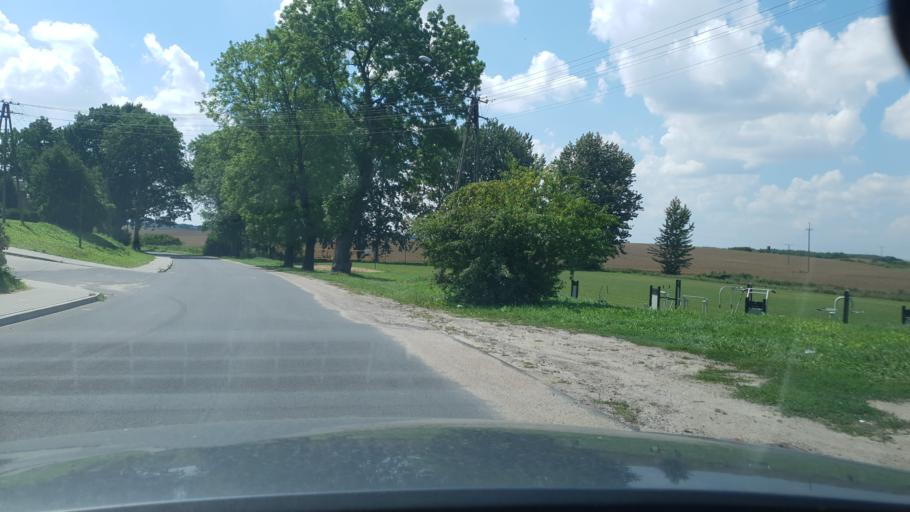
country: PL
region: Kujawsko-Pomorskie
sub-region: Powiat wabrzeski
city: Pluznica
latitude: 53.3451
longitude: 18.8280
